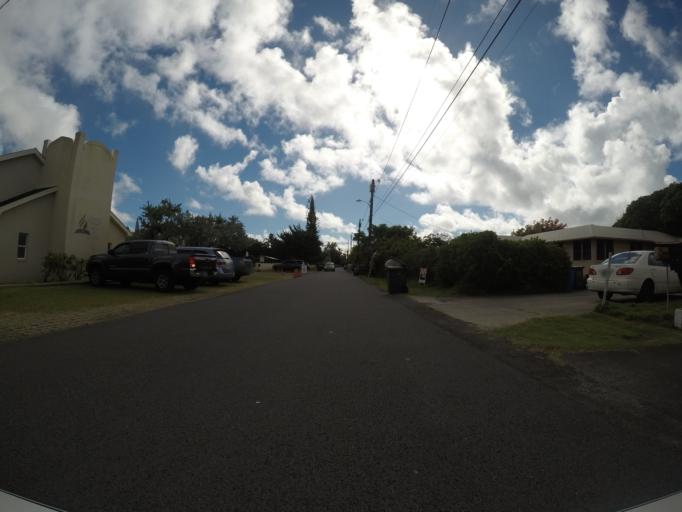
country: US
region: Hawaii
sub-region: Honolulu County
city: Kailua
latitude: 21.4019
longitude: -157.7413
